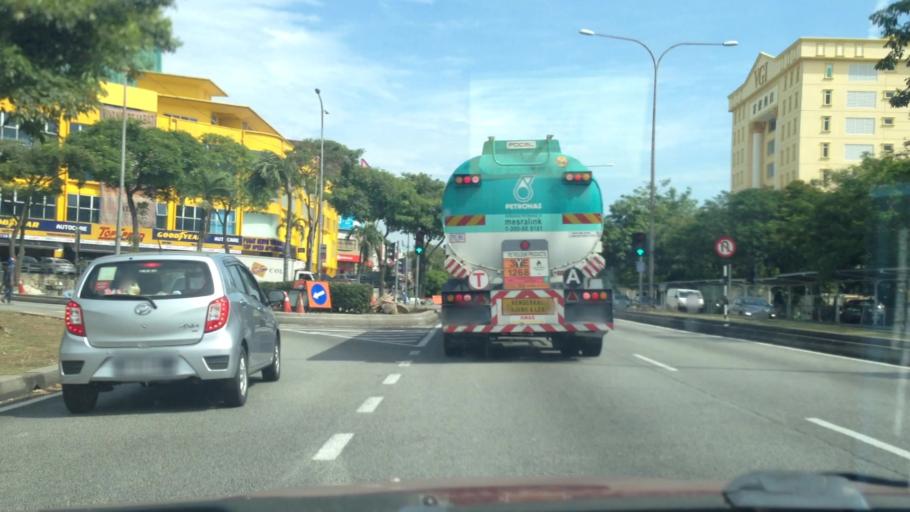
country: MY
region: Selangor
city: Subang Jaya
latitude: 3.0479
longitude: 101.5877
